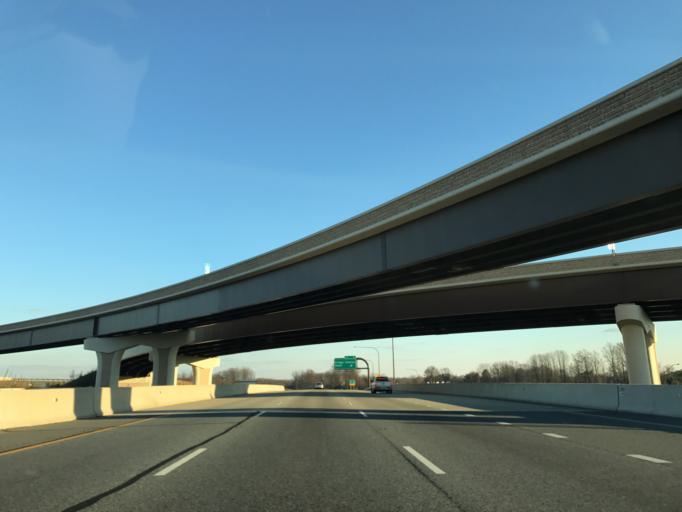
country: US
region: Maryland
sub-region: Montgomery County
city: Fairland
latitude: 39.0783
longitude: -76.9536
